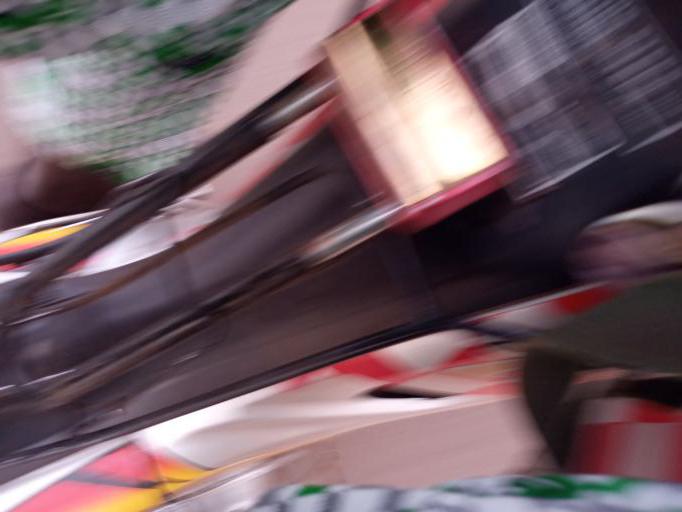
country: ML
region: Bamako
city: Bamako
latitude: 12.6099
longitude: -7.9981
